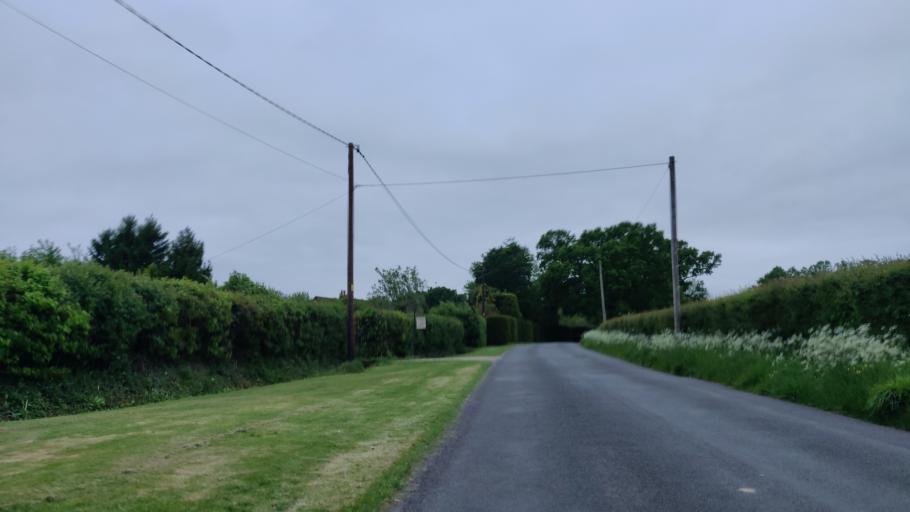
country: GB
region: England
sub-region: West Sussex
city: Southwater
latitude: 51.0265
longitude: -0.3663
